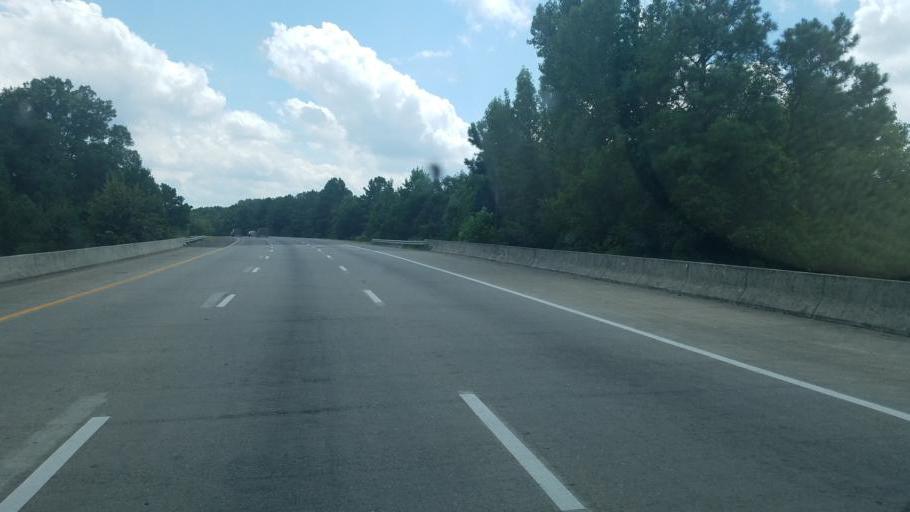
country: US
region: Virginia
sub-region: Henrico County
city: Chamberlayne
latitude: 37.6576
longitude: -77.4456
